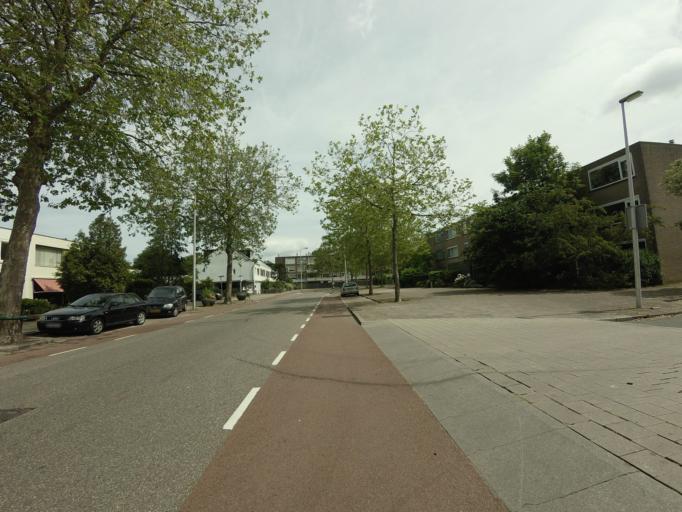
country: NL
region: Utrecht
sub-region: Gemeente Utrecht
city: Utrecht
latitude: 52.1257
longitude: 5.1032
